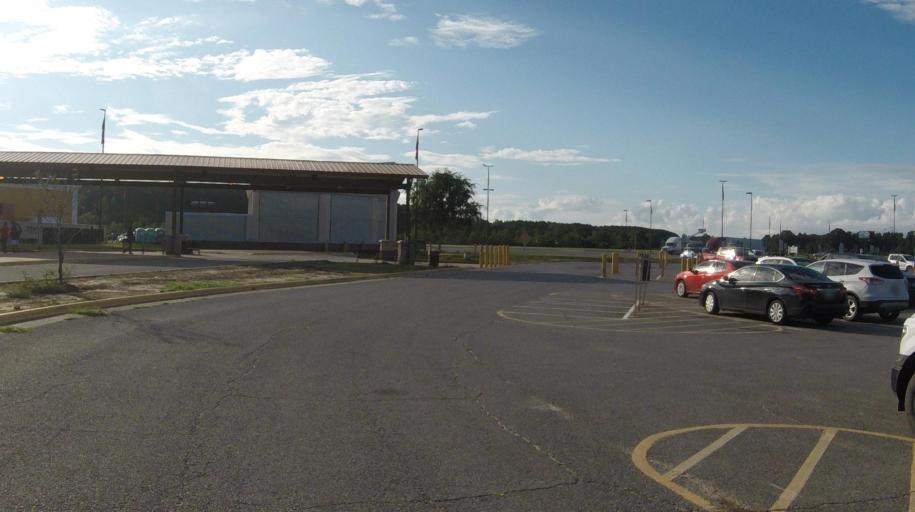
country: US
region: Louisiana
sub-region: Allen Parish
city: Kinder
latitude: 30.5444
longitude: -92.8150
